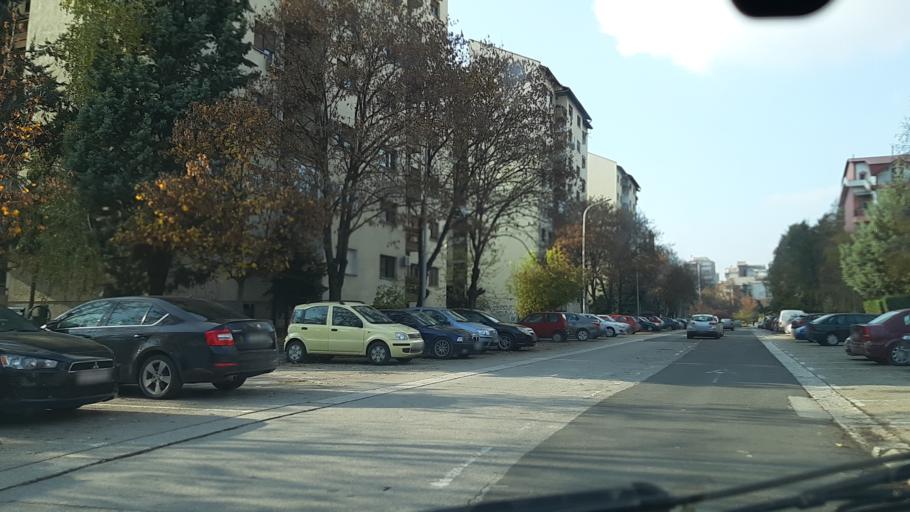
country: MK
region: Kisela Voda
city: Usje
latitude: 41.9814
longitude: 21.4690
